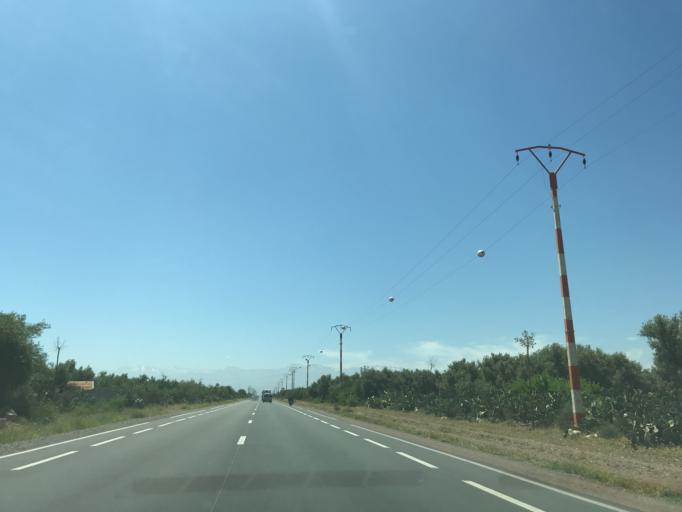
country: MA
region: Marrakech-Tensift-Al Haouz
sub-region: Marrakech
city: Marrakesh
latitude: 31.5412
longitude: -8.0009
